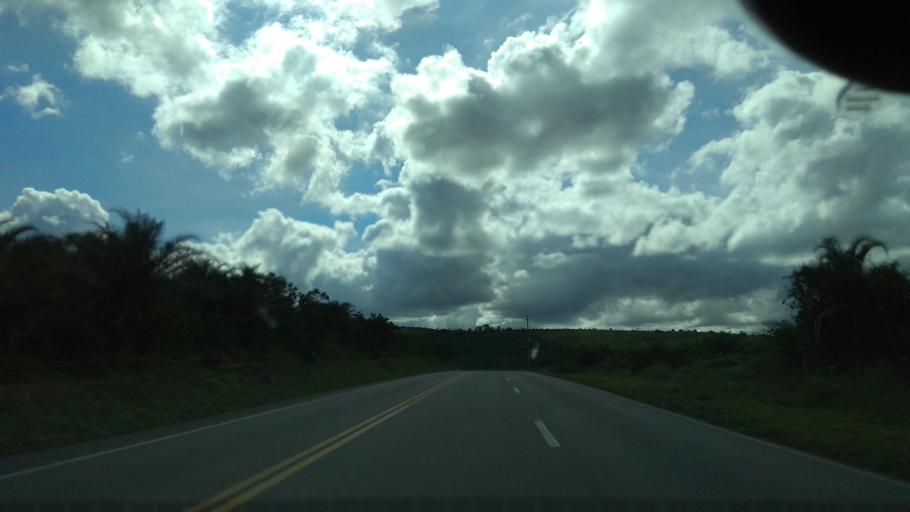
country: BR
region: Bahia
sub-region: Santa Ines
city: Santa Ines
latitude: -13.1245
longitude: -39.9909
